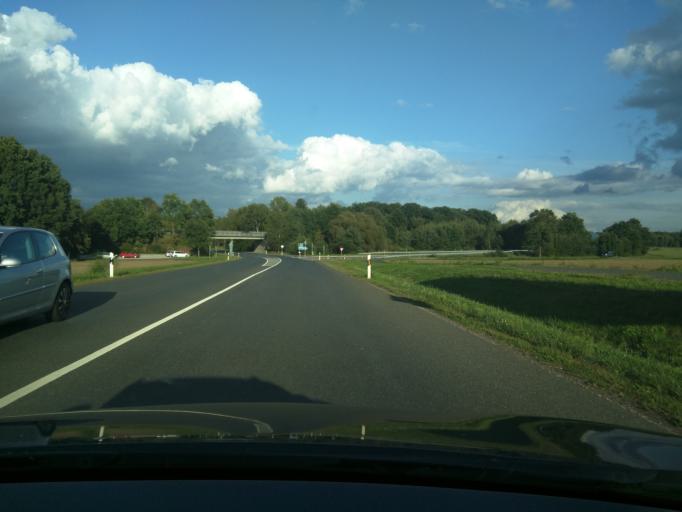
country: DE
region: Bavaria
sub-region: Upper Palatinate
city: Schwandorf in Bayern
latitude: 49.3460
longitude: 12.1388
